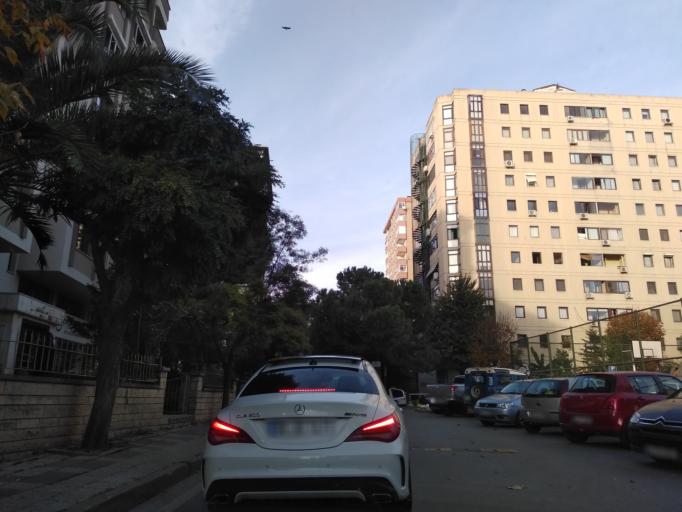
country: TR
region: Istanbul
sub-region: Atasehir
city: Atasehir
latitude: 40.9771
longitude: 29.0912
